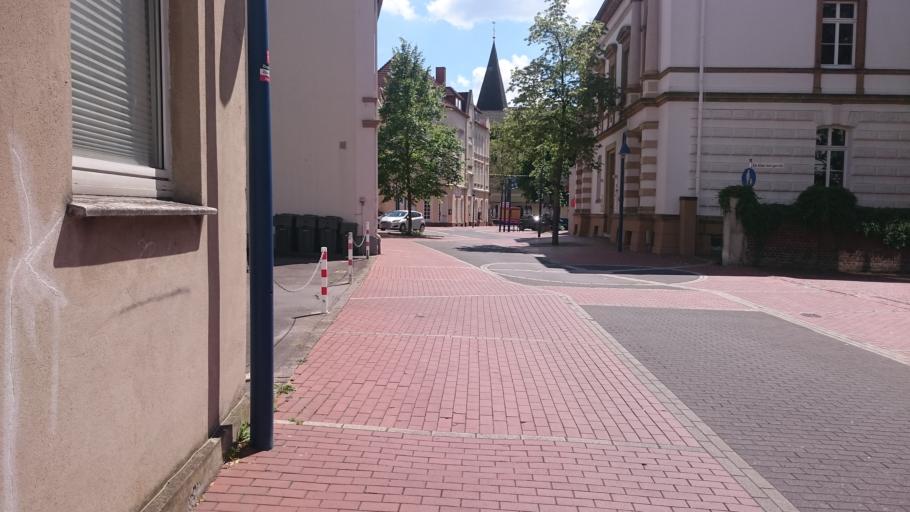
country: DE
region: North Rhine-Westphalia
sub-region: Regierungsbezirk Detmold
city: Lage
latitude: 51.9919
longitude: 8.7917
